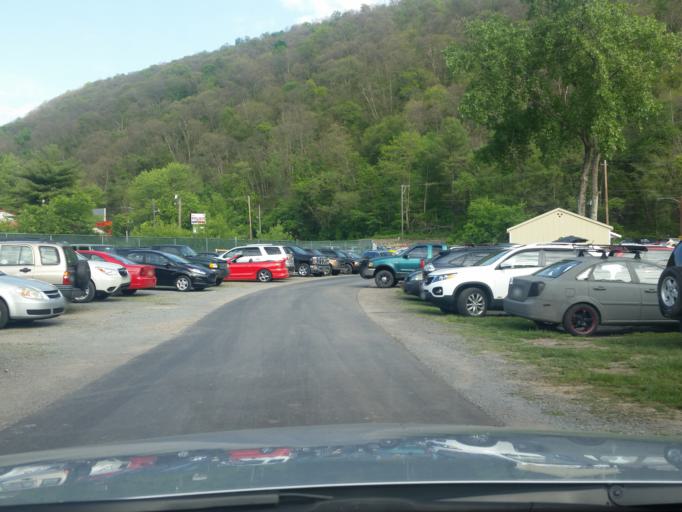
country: US
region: Pennsylvania
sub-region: Luzerne County
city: Nanticoke
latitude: 41.2139
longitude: -76.0407
